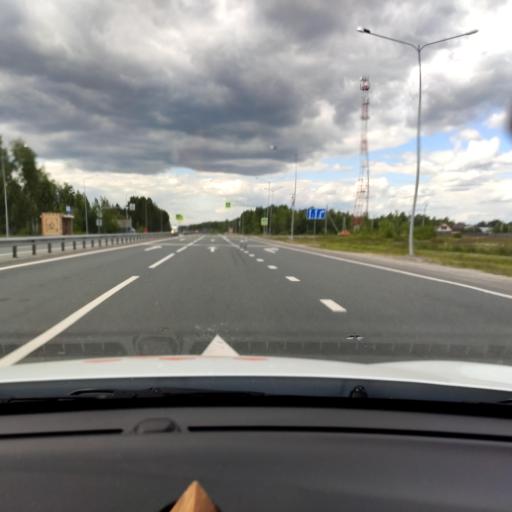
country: RU
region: Mariy-El
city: Surok
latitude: 56.4400
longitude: 48.1127
